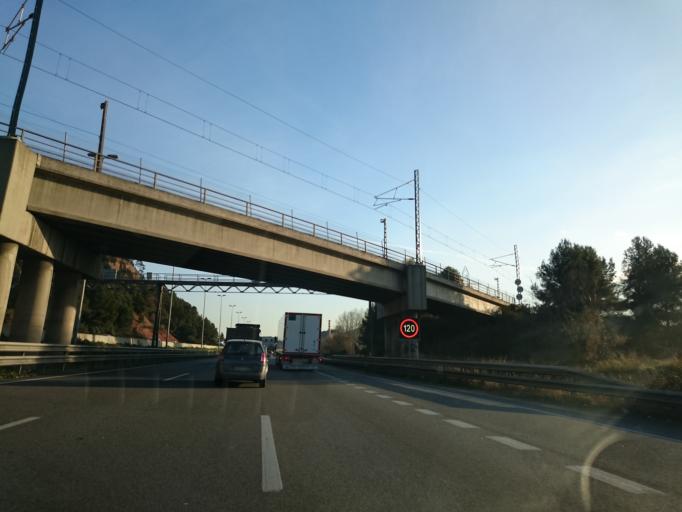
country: ES
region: Catalonia
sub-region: Provincia de Barcelona
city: Castellbisbal
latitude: 41.4631
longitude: 1.9800
